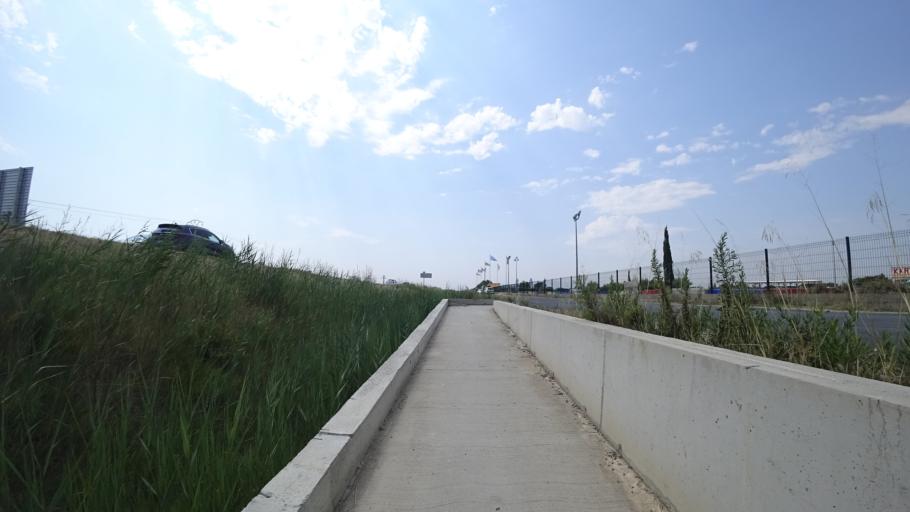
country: FR
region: Languedoc-Roussillon
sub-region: Departement des Pyrenees-Orientales
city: Torreilles
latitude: 42.7596
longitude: 3.0197
